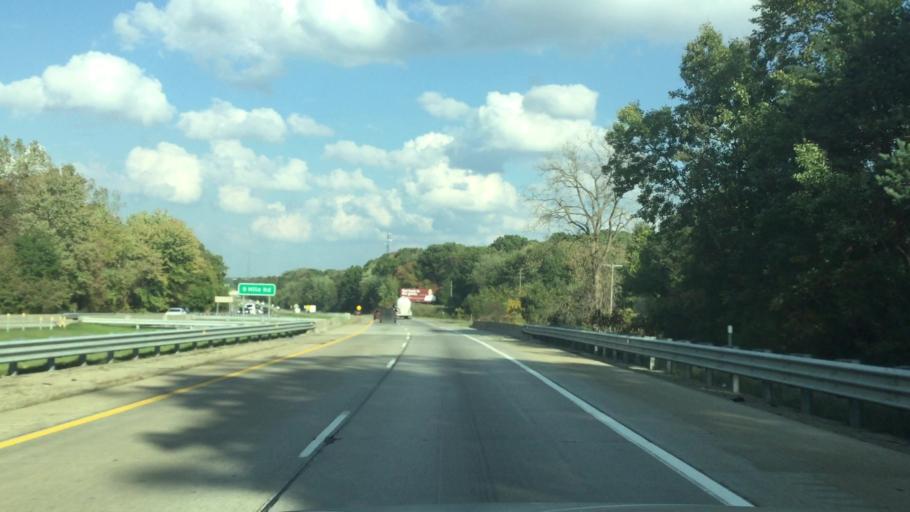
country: US
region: Michigan
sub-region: Calhoun County
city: Brownlee Park
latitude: 42.2869
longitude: -85.1212
